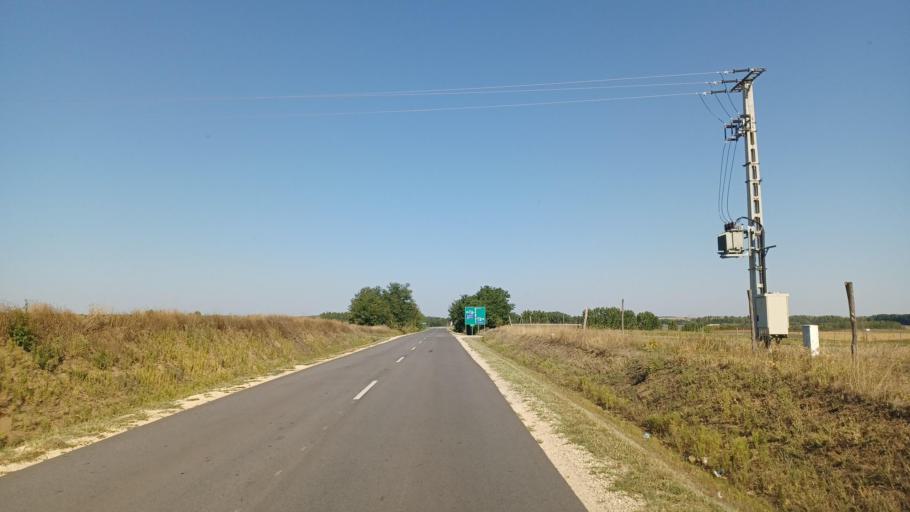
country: HU
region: Tolna
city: Paks
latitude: 46.6682
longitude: 18.8203
